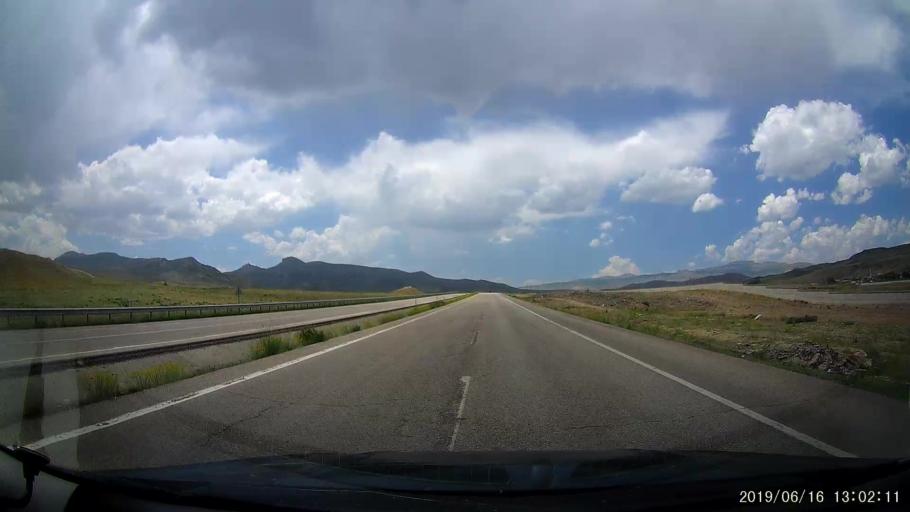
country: TR
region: Agri
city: Sulucem
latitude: 39.5732
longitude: 43.8227
